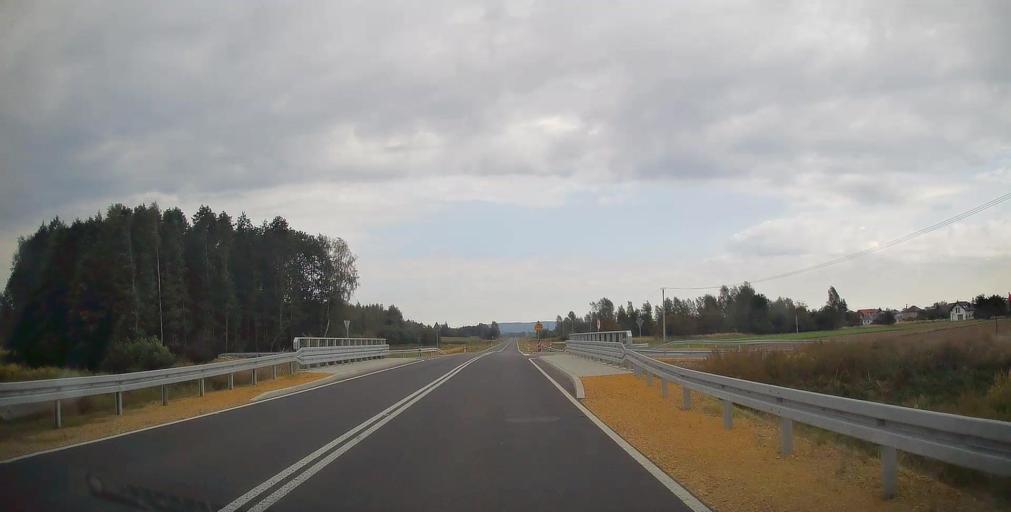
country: PL
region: Lesser Poland Voivodeship
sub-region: Powiat oswiecimski
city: Zator
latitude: 50.0057
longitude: 19.4234
